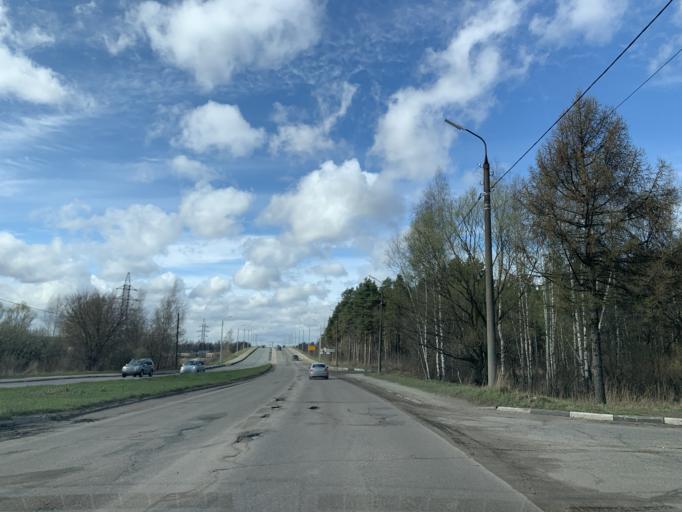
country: RU
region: Jaroslavl
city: Yaroslavl
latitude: 57.6615
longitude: 39.9577
